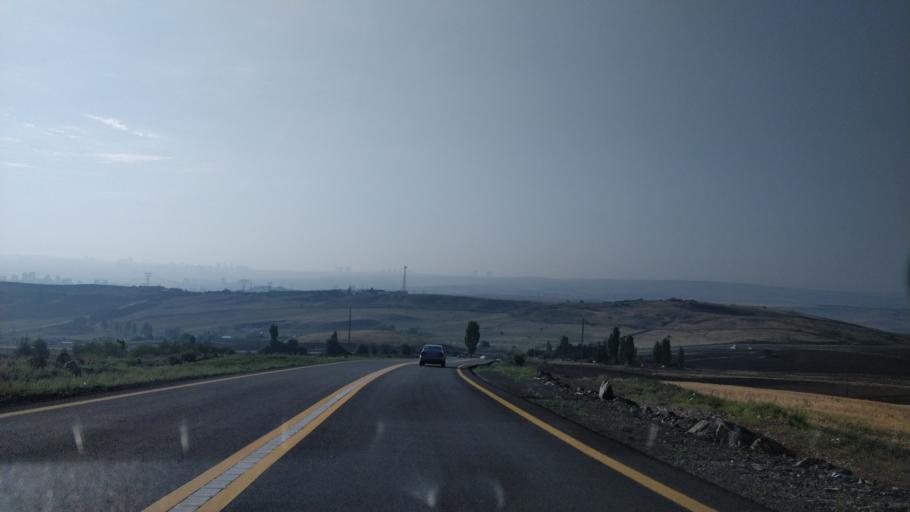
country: TR
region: Ankara
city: Etimesgut
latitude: 39.8622
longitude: 32.5772
